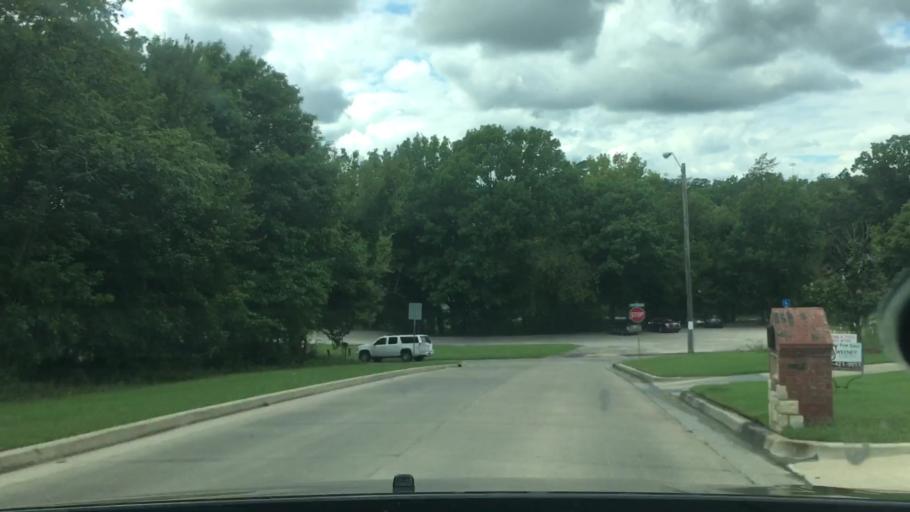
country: US
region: Oklahoma
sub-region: Pontotoc County
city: Ada
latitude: 34.7576
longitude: -96.6532
